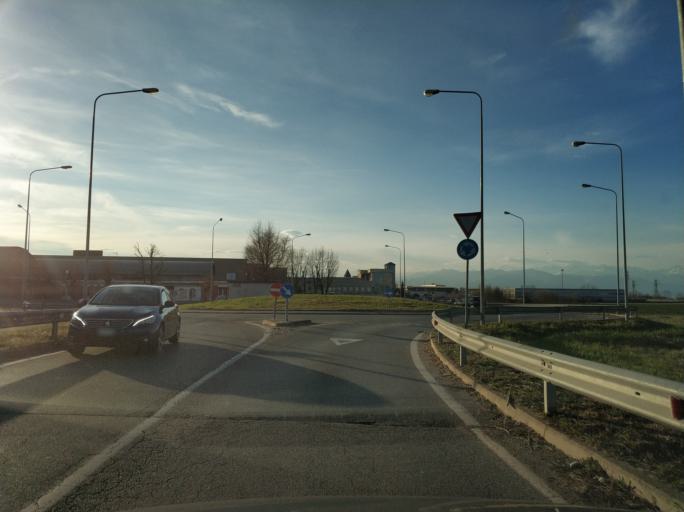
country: IT
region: Piedmont
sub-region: Provincia di Torino
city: Volpiano
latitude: 45.1923
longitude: 7.8021
